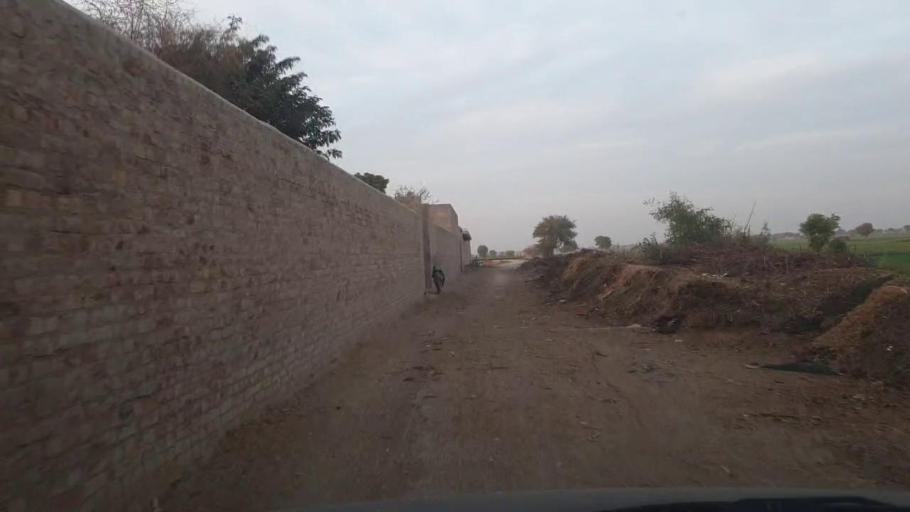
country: PK
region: Sindh
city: Shahpur Chakar
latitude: 26.0759
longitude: 68.5324
